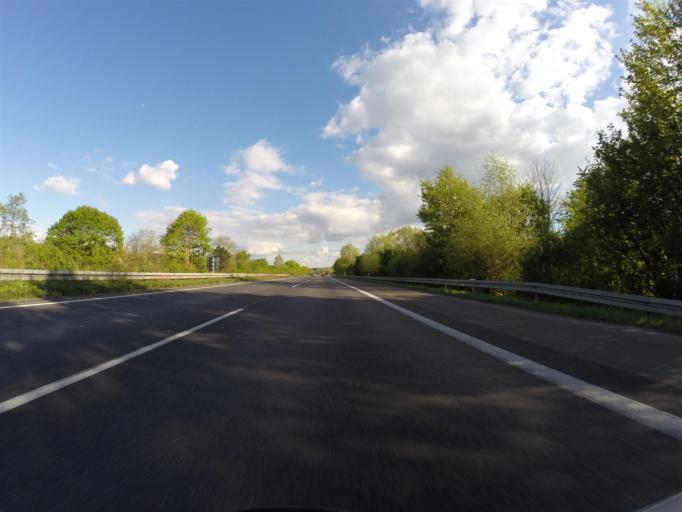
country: DE
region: Saarland
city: Merzig
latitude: 49.4204
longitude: 6.6344
